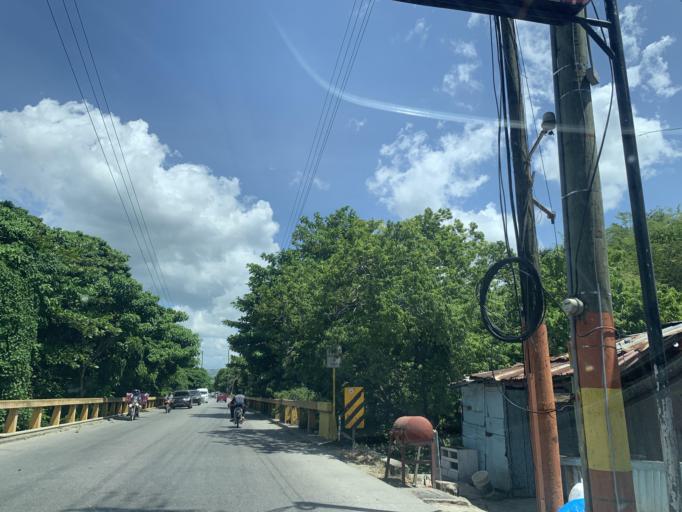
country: DO
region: Espaillat
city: Jamao al Norte
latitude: 19.6739
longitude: -70.3733
